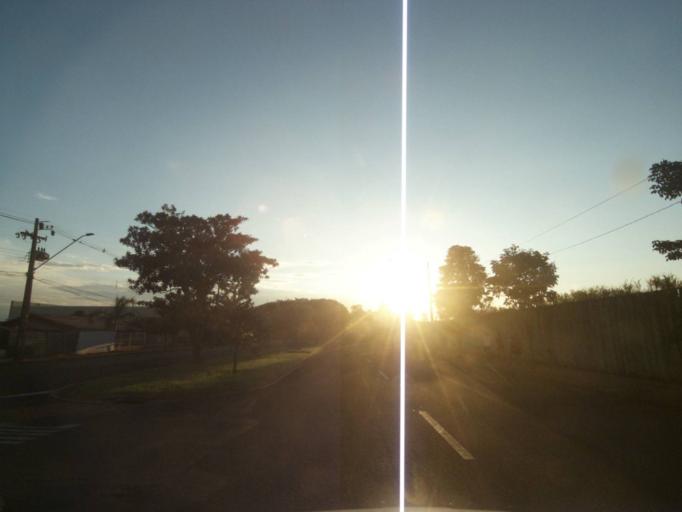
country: BR
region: Parana
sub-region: Londrina
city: Londrina
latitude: -23.3604
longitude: -51.1582
